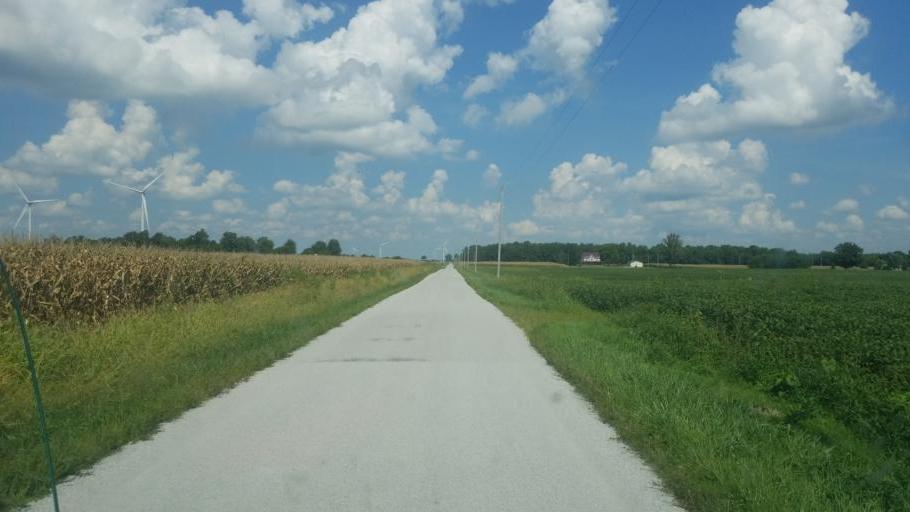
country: US
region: Ohio
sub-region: Hardin County
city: Ada
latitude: 40.7573
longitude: -83.7096
